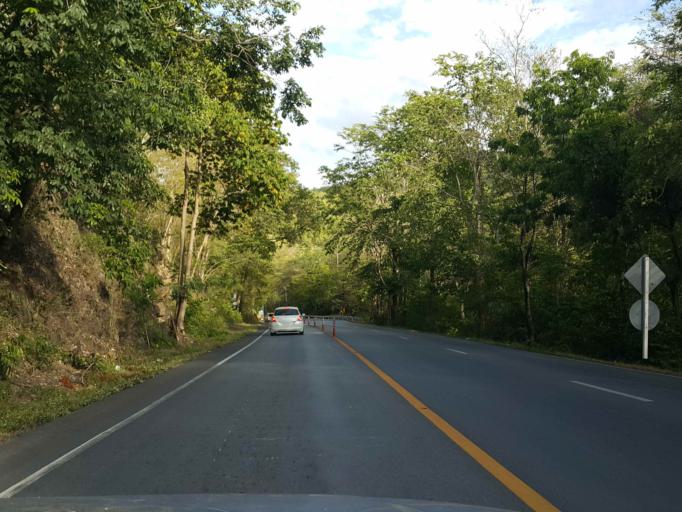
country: TH
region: Tak
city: Tak
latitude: 16.8102
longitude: 98.9827
